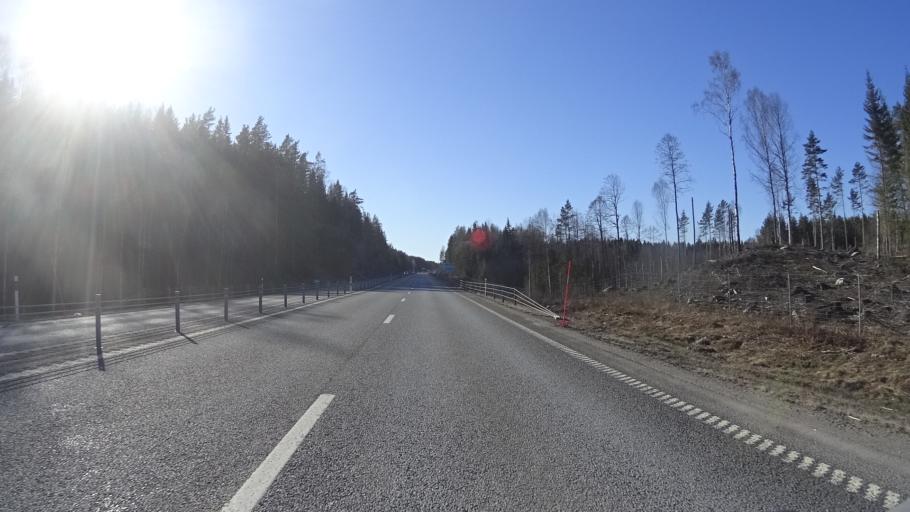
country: SE
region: Vaermland
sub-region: Arvika Kommun
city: Arvika
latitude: 59.6449
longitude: 12.7206
